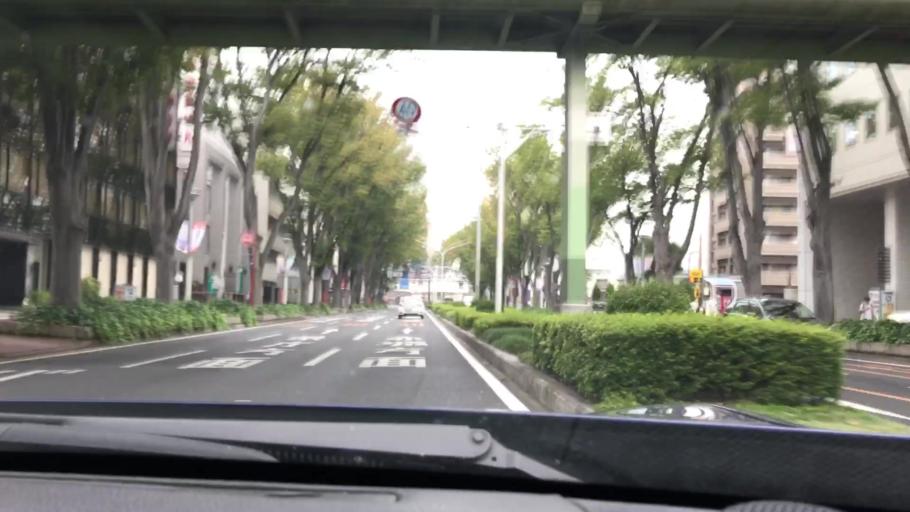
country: JP
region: Gunma
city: Maebashi-shi
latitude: 36.3863
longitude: 139.0726
